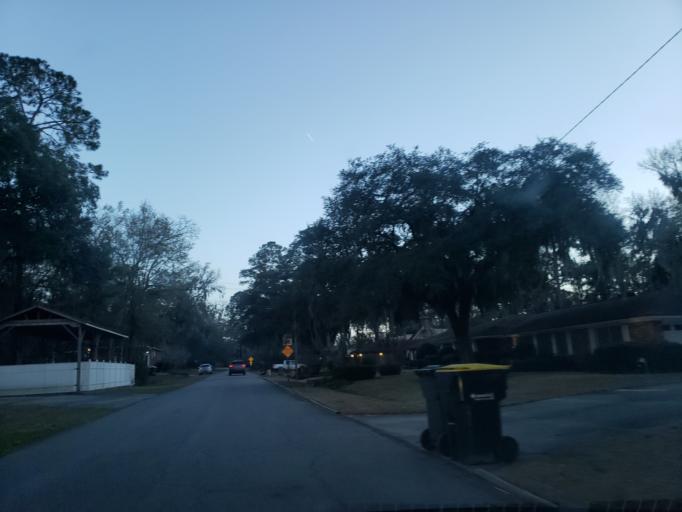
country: US
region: Georgia
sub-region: Chatham County
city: Thunderbolt
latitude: 32.0191
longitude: -81.0859
